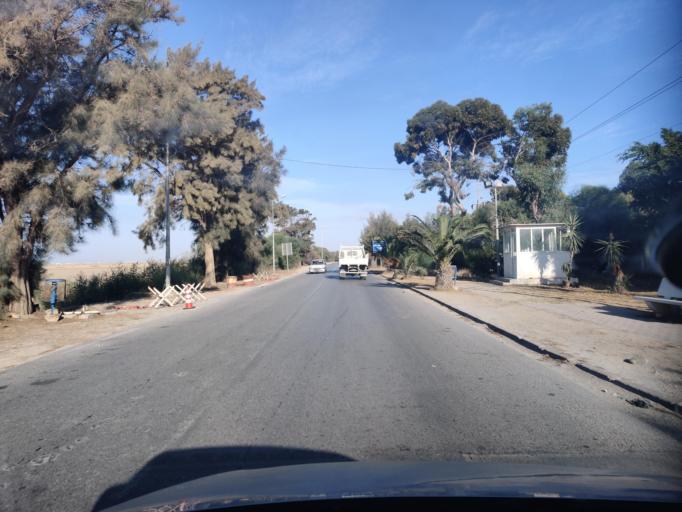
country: TN
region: Tunis
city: Al Marsa
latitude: 36.9399
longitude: 10.2507
